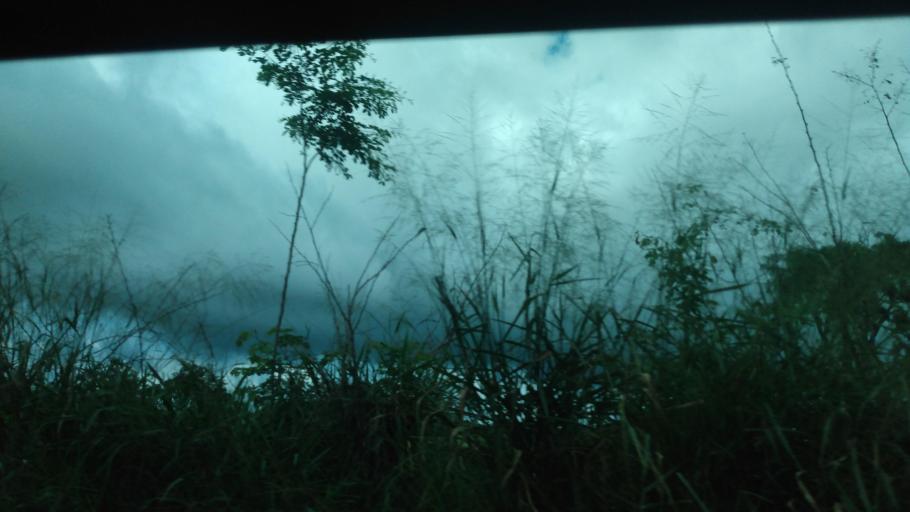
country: BR
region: Pernambuco
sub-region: Quipapa
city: Quipapa
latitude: -8.8102
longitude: -36.0094
